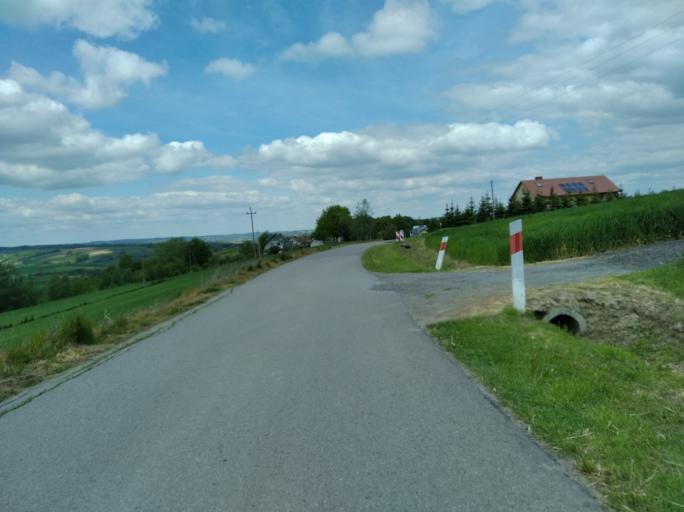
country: PL
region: Subcarpathian Voivodeship
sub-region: Powiat ropczycko-sedziszowski
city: Wielopole Skrzynskie
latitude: 49.9272
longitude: 21.6024
